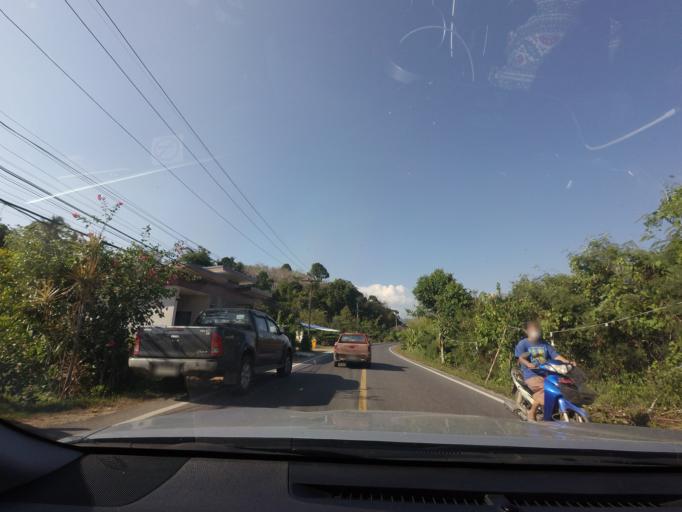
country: TH
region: Phangnga
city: Takua Thung
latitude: 8.2714
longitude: 98.3716
